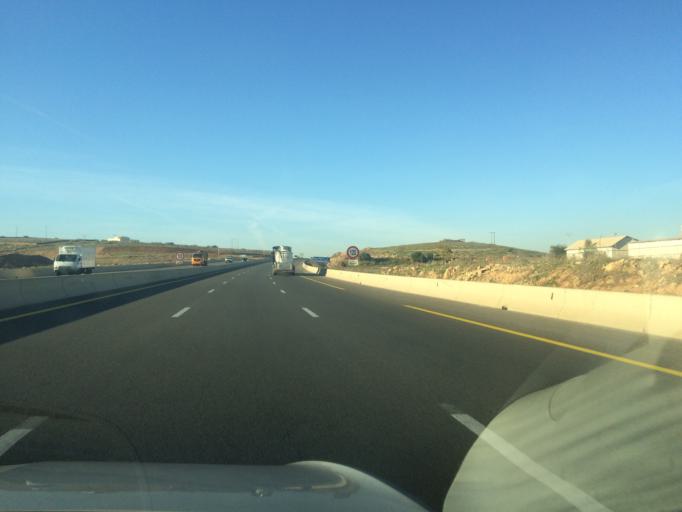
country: DZ
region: Chlef
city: Oued Sly
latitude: 36.0762
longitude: 1.1799
